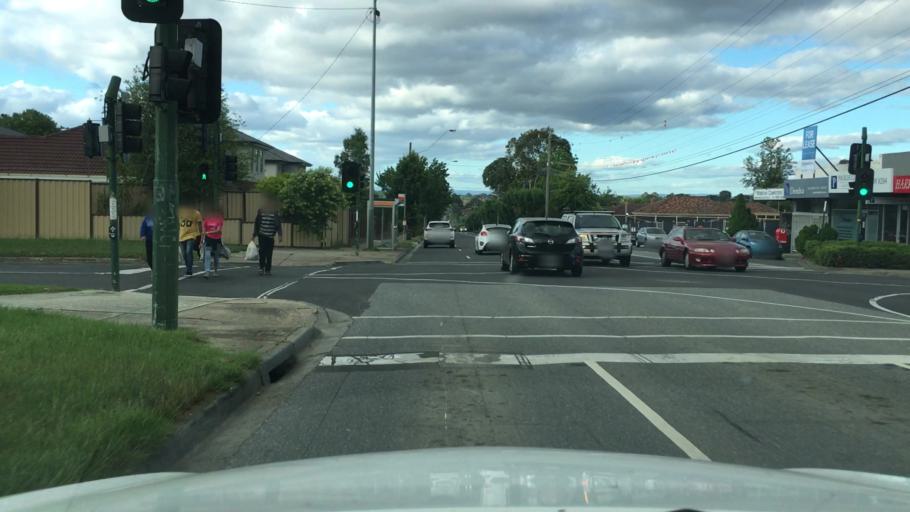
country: AU
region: Victoria
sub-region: Whitehorse
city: Burwood
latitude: -37.8459
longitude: 145.1334
